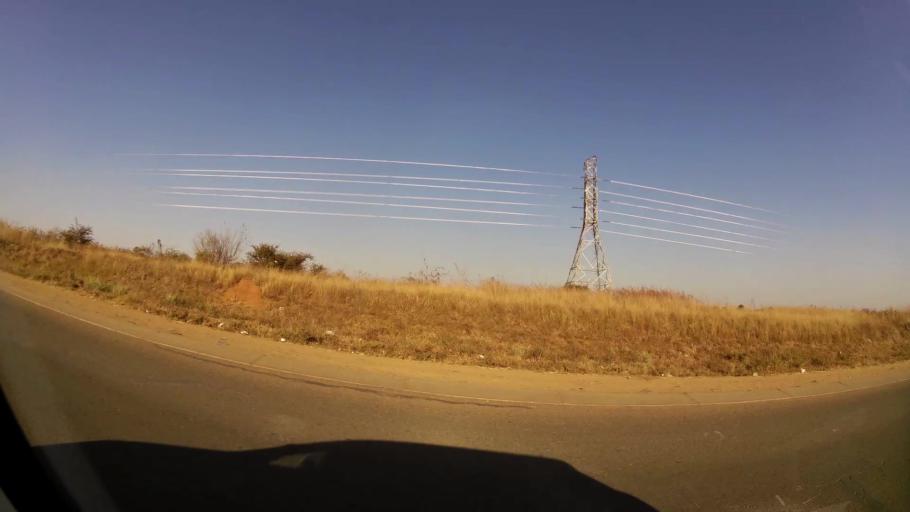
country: ZA
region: Gauteng
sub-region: City of Tshwane Metropolitan Municipality
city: Cullinan
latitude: -25.7324
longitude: 28.3984
